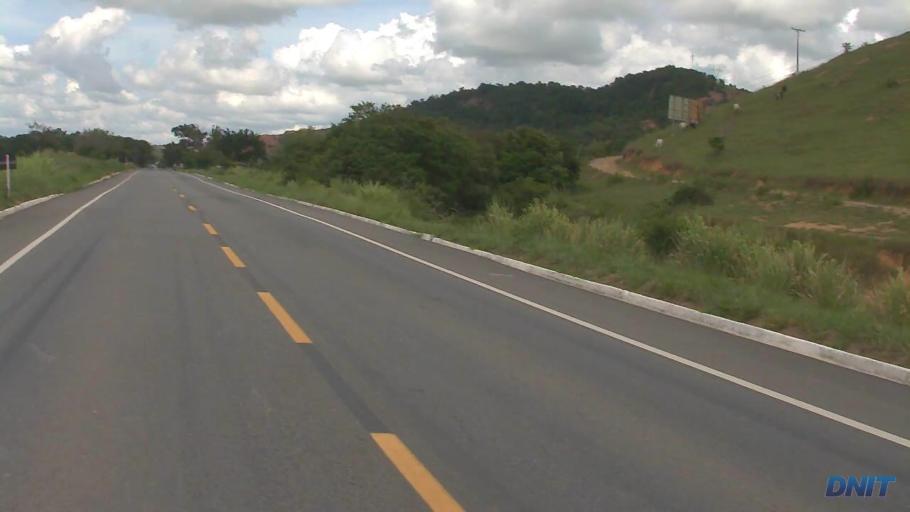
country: BR
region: Minas Gerais
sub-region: Governador Valadares
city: Governador Valadares
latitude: -18.9453
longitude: -42.0657
